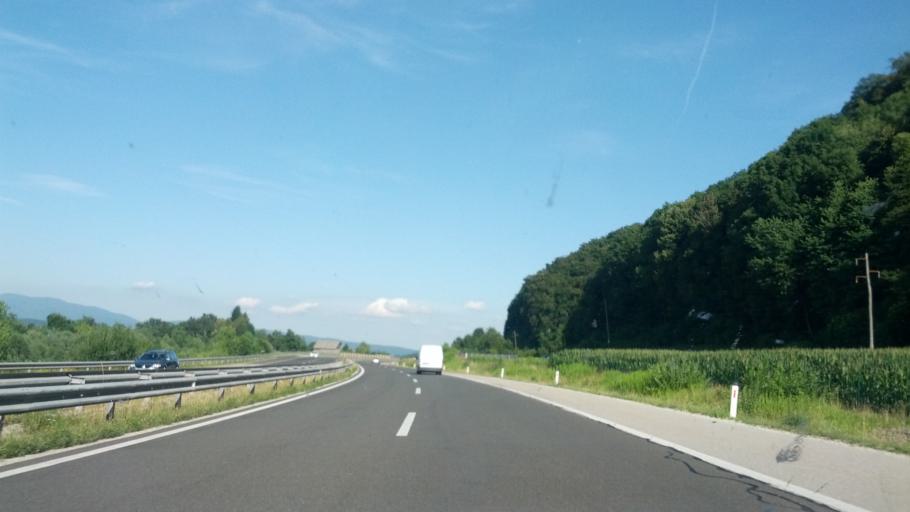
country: HR
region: Zagrebacka
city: Bregana
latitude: 45.8716
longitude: 15.6581
